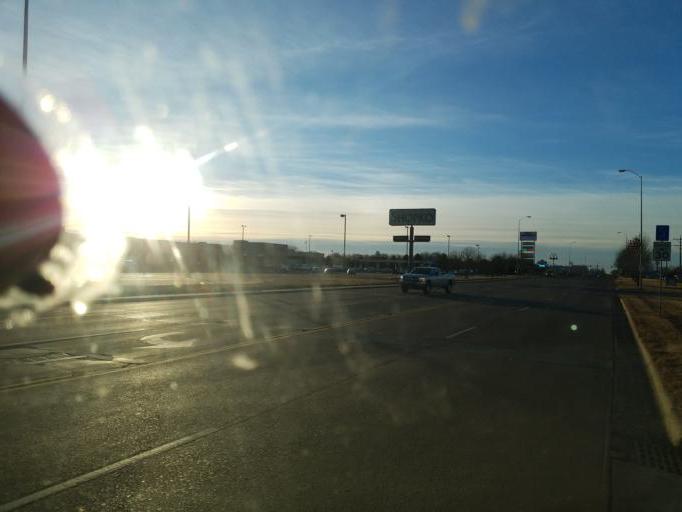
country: US
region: South Dakota
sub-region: Davison County
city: Mitchell
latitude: 43.7289
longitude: -98.0259
